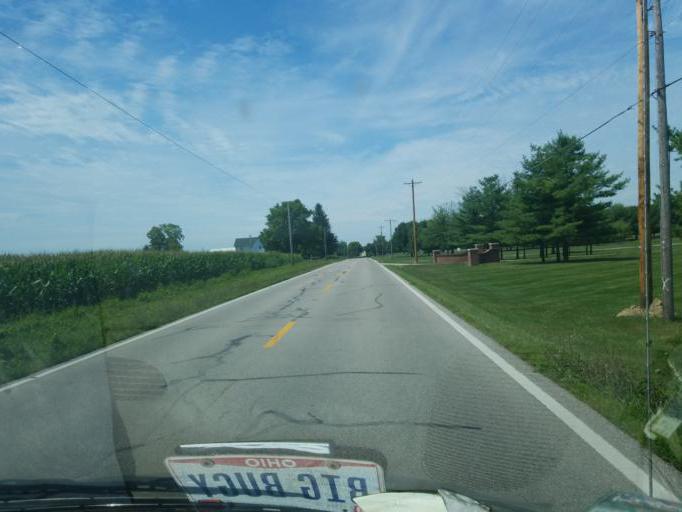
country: US
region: Ohio
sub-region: Franklin County
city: Grove City
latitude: 39.8748
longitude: -83.1617
